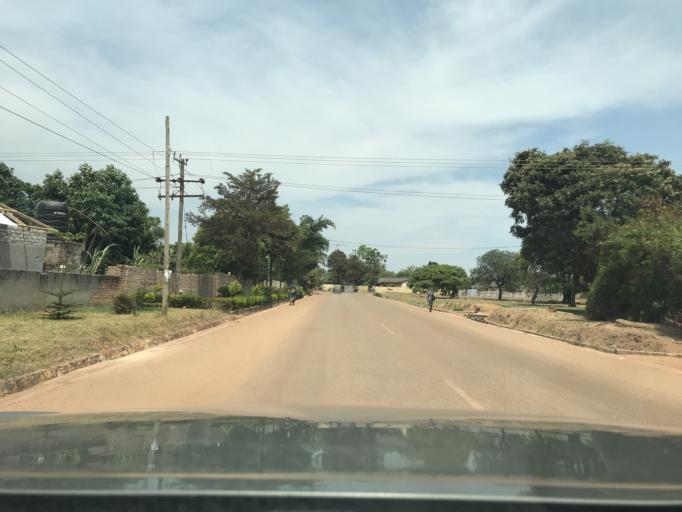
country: ZM
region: Northern
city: Kasama
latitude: -10.2034
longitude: 31.1867
